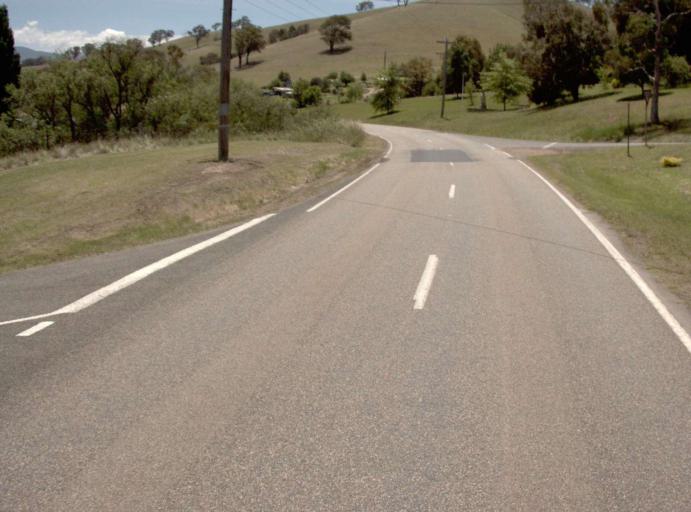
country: AU
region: Victoria
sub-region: East Gippsland
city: Bairnsdale
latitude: -37.3755
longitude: 147.8357
